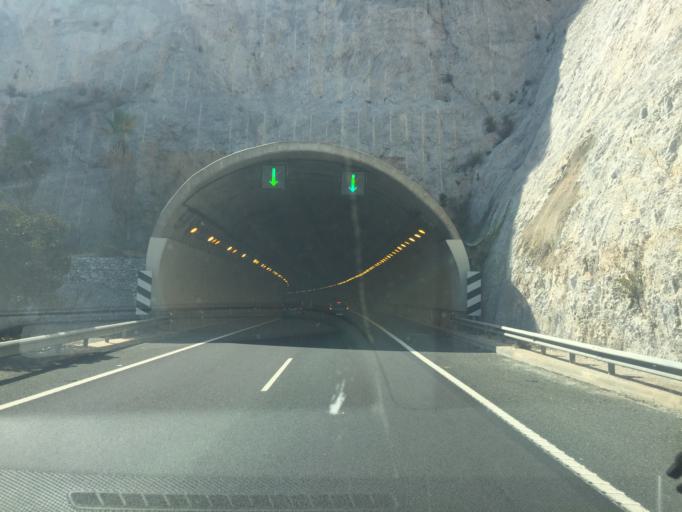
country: ES
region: Andalusia
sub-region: Provincia de Malaga
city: Nerja
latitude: 36.7659
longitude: -3.8626
